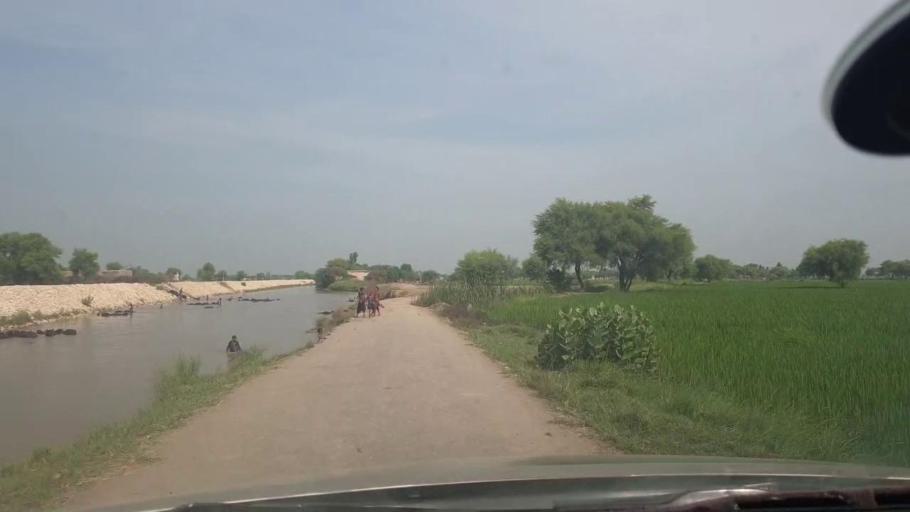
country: PK
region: Sindh
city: Jacobabad
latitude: 28.2917
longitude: 68.4805
